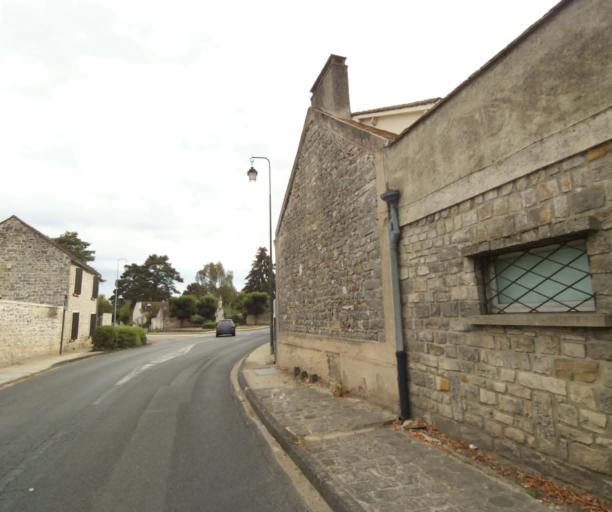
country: FR
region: Ile-de-France
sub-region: Departement de Seine-et-Marne
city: Arbonne-la-Foret
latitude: 48.4117
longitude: 2.5648
